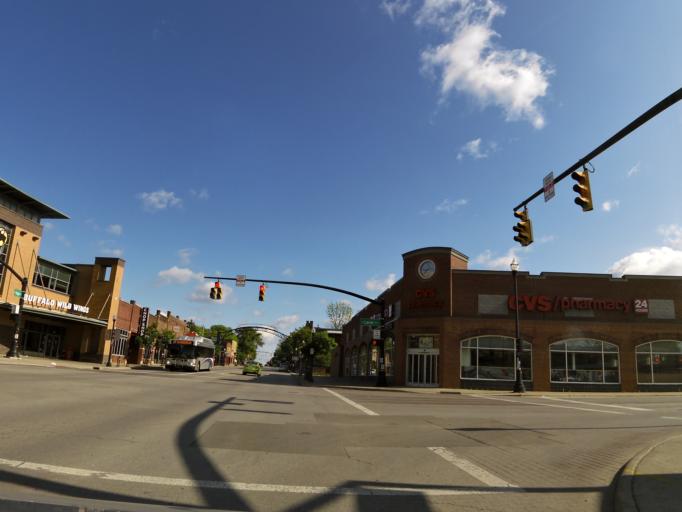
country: US
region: Ohio
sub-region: Franklin County
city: Grandview Heights
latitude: 40.0059
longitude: -83.0091
